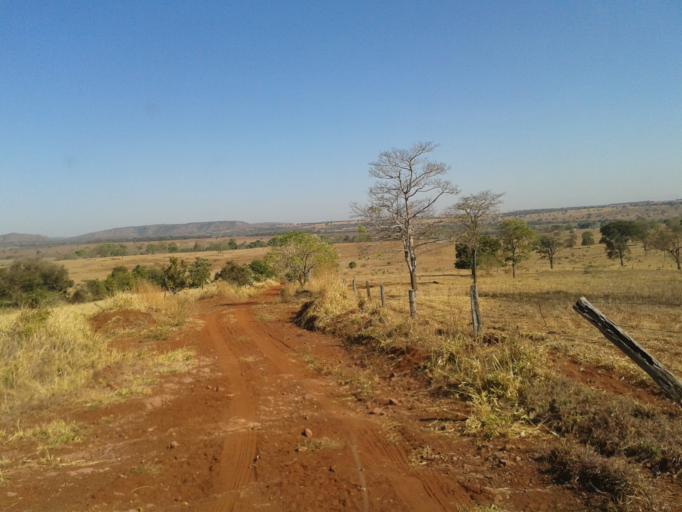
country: BR
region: Minas Gerais
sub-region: Santa Vitoria
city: Santa Vitoria
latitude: -19.0469
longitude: -49.9432
